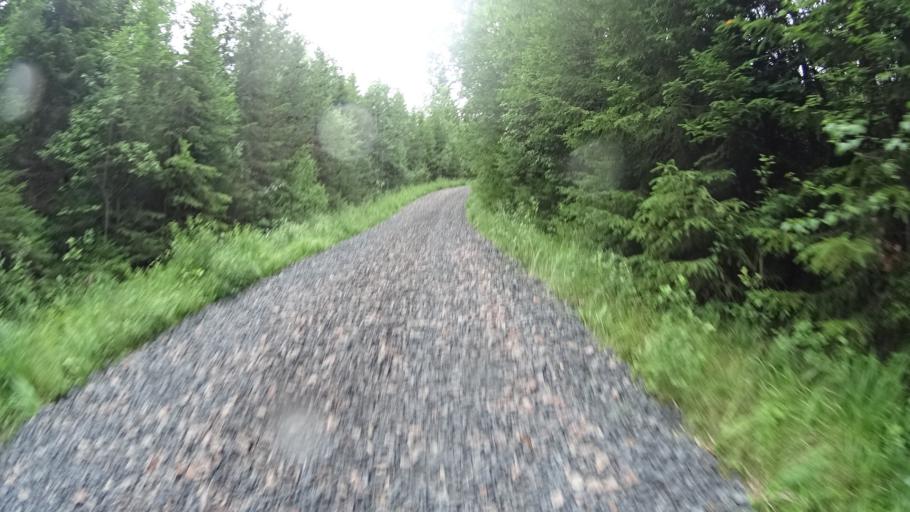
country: FI
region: Uusimaa
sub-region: Helsinki
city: Karkkila
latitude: 60.5844
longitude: 24.1558
